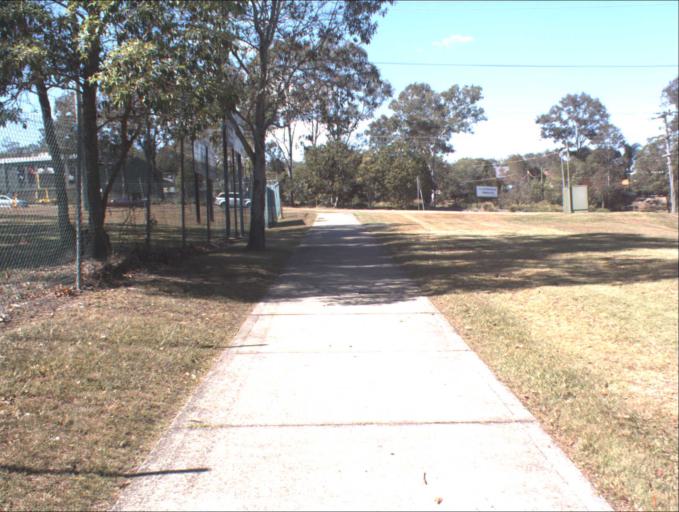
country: AU
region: Queensland
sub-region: Logan
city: Beenleigh
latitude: -27.7212
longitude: 153.1958
